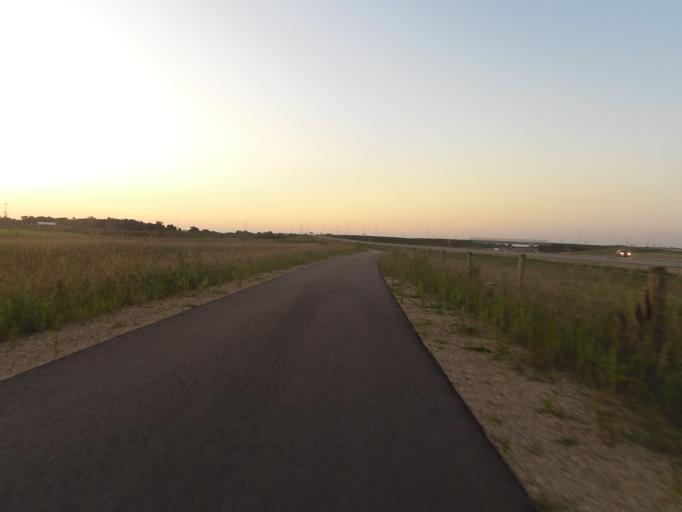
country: US
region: Minnesota
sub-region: Washington County
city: Stillwater
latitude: 45.0560
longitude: -92.7803
